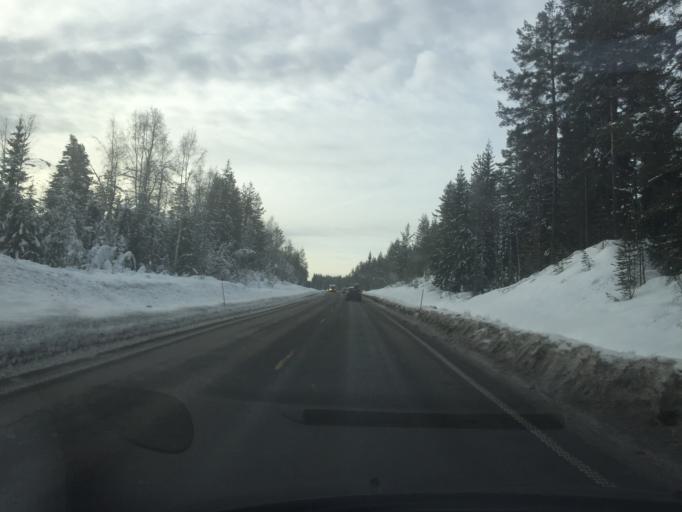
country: NO
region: Hedmark
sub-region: Trysil
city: Innbygda
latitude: 61.2578
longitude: 12.3040
